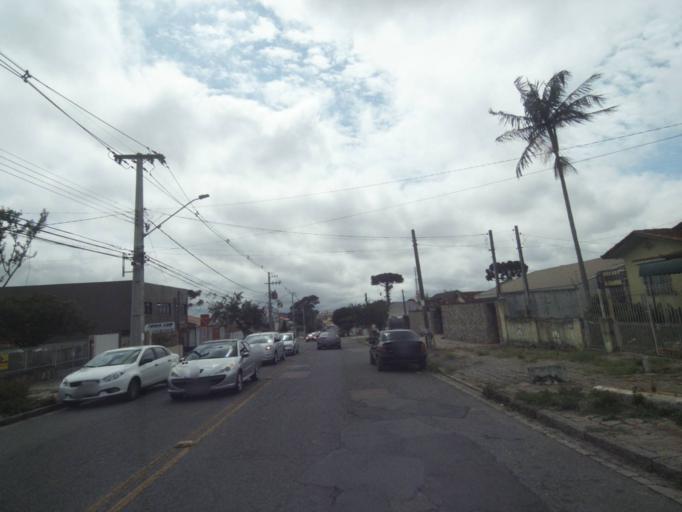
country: BR
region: Parana
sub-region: Pinhais
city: Pinhais
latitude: -25.4388
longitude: -49.2322
